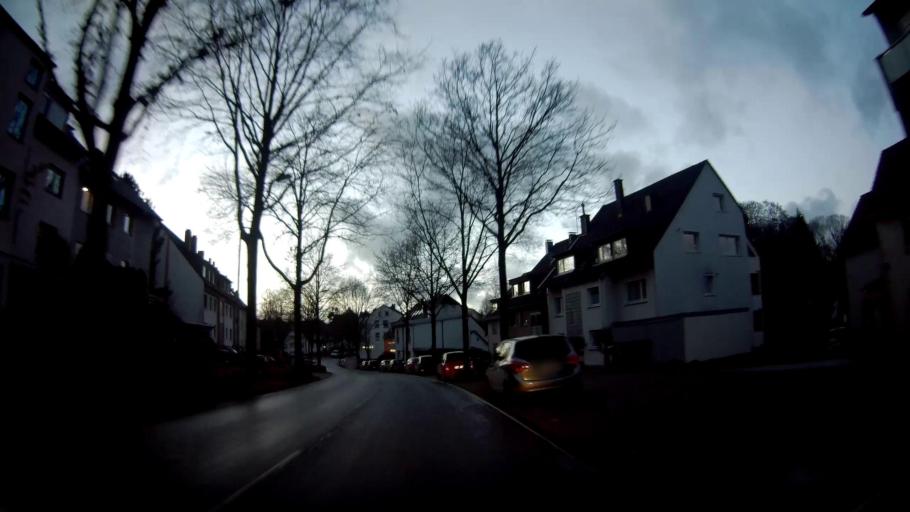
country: DE
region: North Rhine-Westphalia
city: Castrop-Rauxel
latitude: 51.5018
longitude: 7.2786
